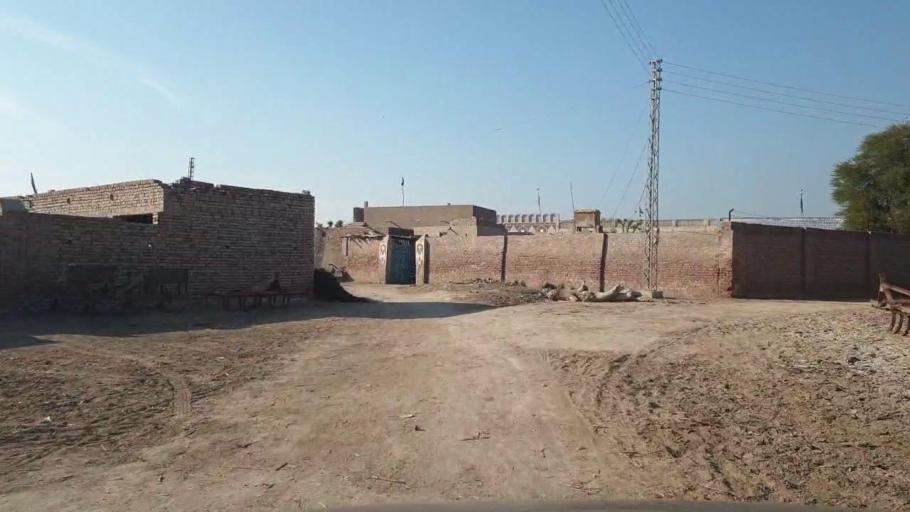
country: PK
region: Sindh
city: Shahpur Chakar
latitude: 26.1721
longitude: 68.6601
